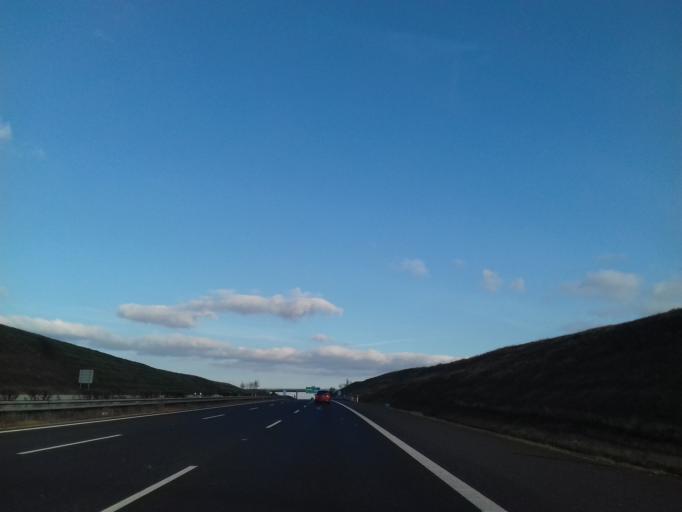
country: CZ
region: Plzensky
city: Dobrany
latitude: 49.6793
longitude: 13.3391
